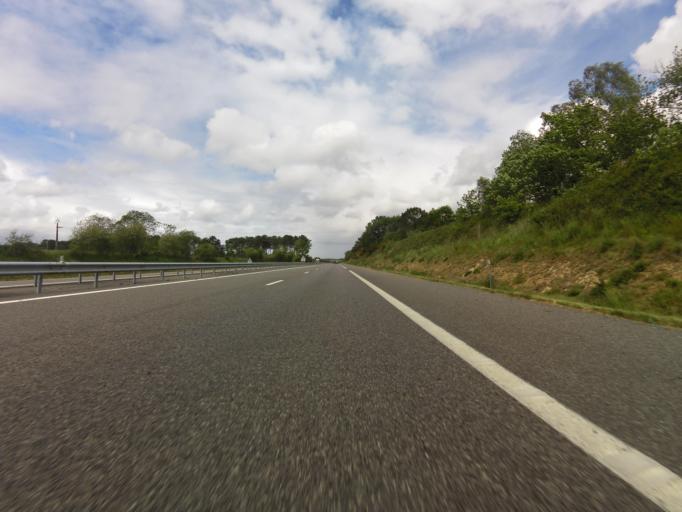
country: FR
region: Brittany
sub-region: Departement du Morbihan
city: Allaire
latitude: 47.6189
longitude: -2.1562
